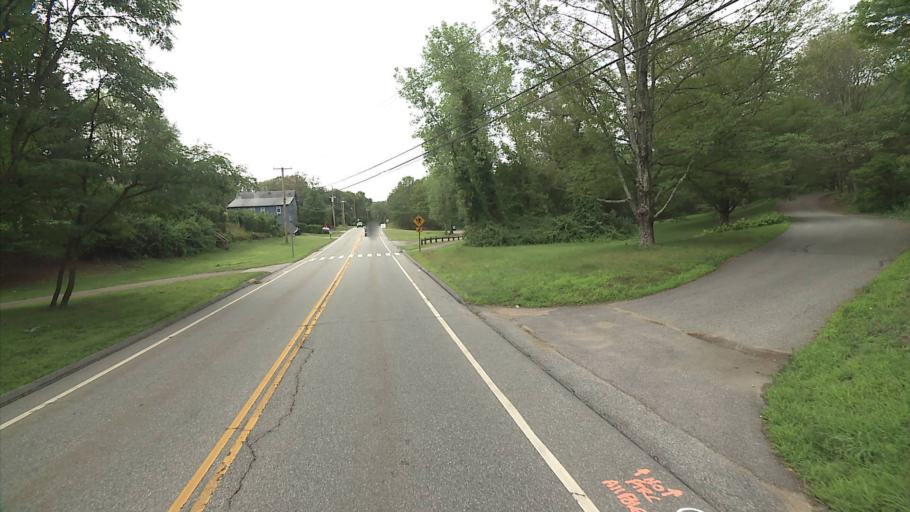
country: US
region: Connecticut
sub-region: New London County
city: Colchester
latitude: 41.5854
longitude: -72.3999
